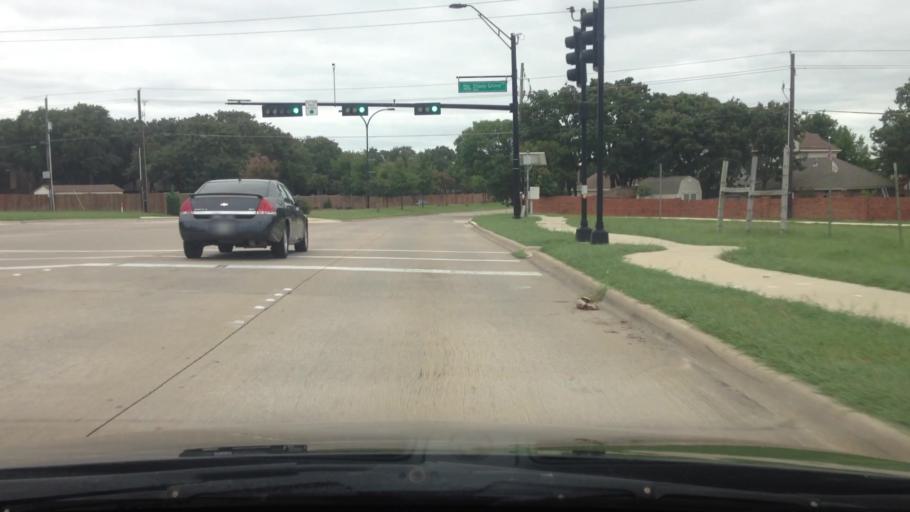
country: US
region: Texas
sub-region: Tarrant County
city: Keller
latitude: 32.9103
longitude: -97.2324
